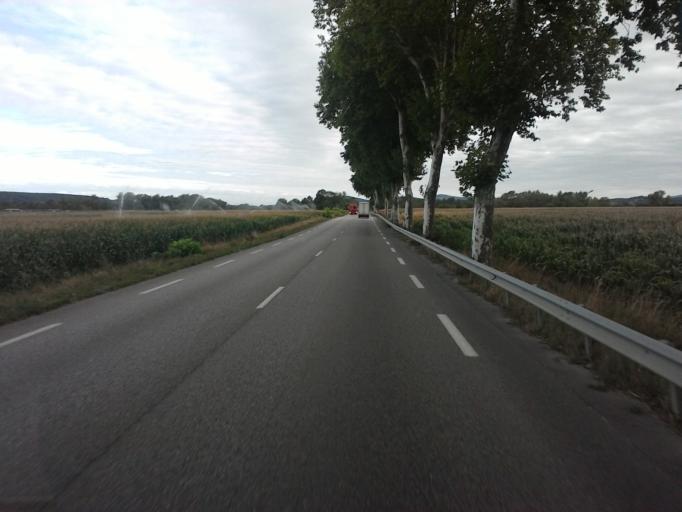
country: FR
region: Rhone-Alpes
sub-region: Departement de l'Ain
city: Ambronay
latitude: 46.0218
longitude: 5.3393
